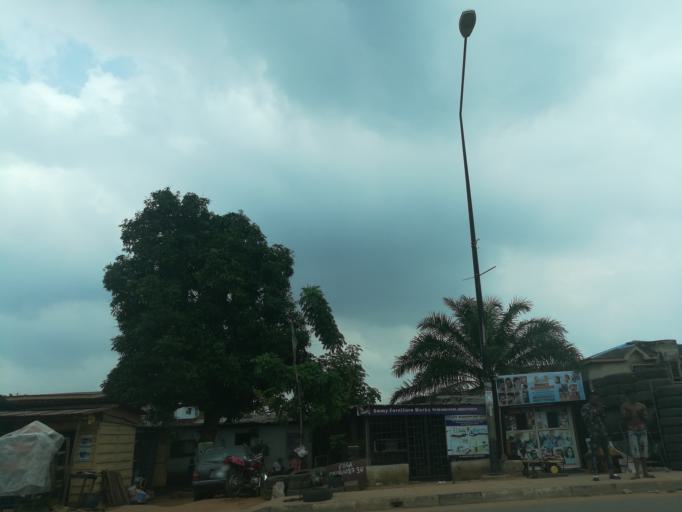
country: NG
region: Lagos
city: Ikorodu
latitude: 6.6179
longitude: 3.5158
